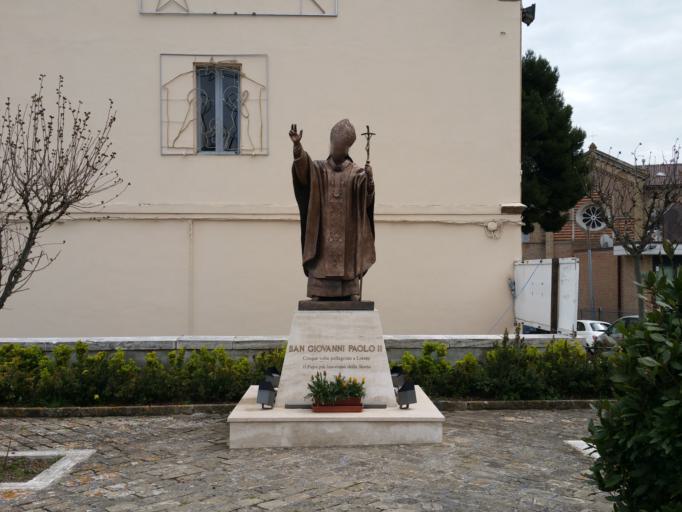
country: IT
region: The Marches
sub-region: Provincia di Ancona
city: Loreto
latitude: 43.4414
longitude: 13.6119
